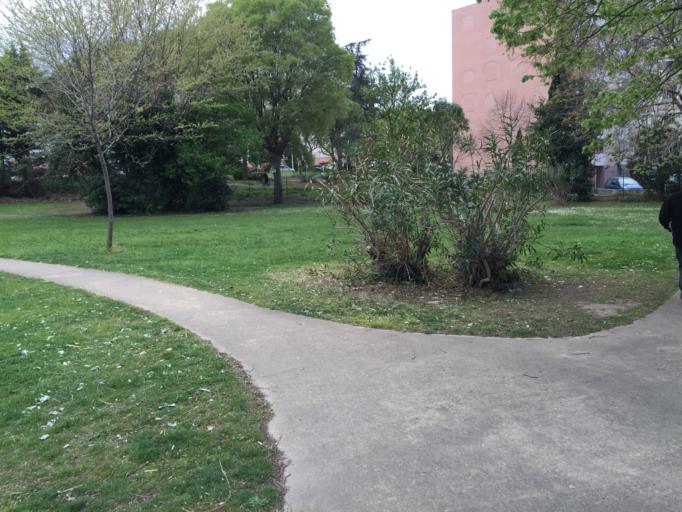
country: FR
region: Provence-Alpes-Cote d'Azur
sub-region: Departement des Bouches-du-Rhone
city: Marseille 09
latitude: 43.2477
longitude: 5.3961
